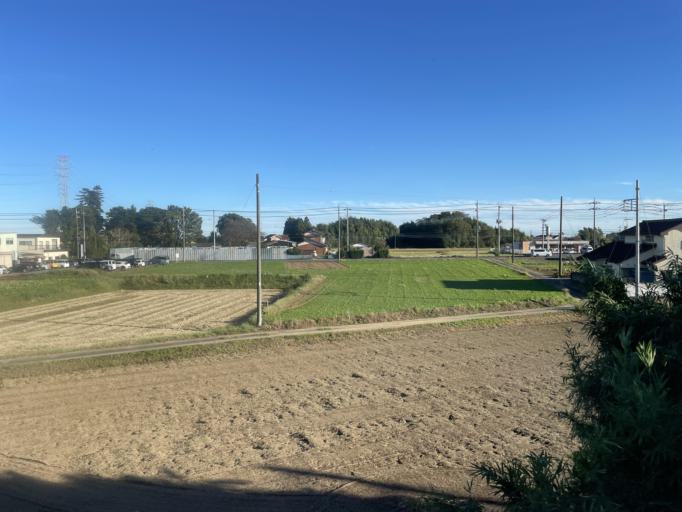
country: JP
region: Tochigi
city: Fujioka
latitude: 36.2798
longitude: 139.6587
